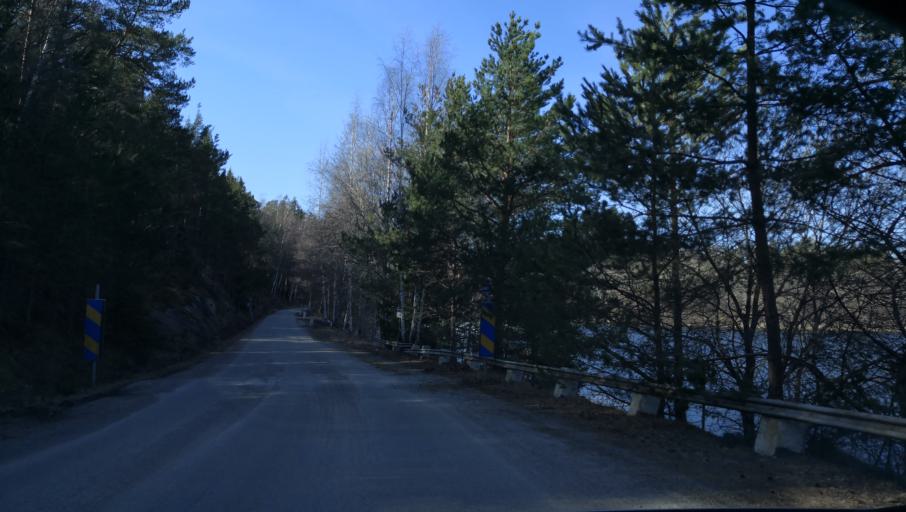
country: SE
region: Stockholm
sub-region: Varmdo Kommun
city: Mortnas
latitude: 59.2966
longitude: 18.4180
